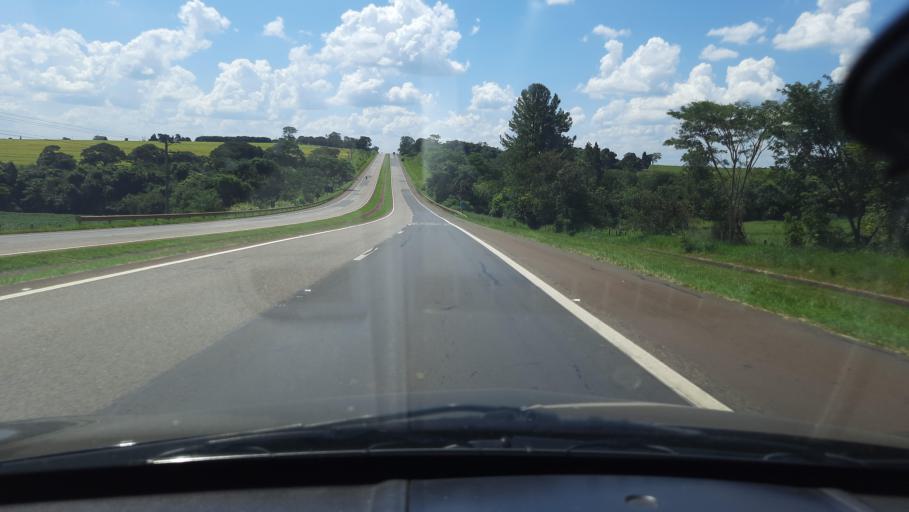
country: BR
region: Sao Paulo
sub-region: Casa Branca
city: Casa Branca
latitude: -21.7327
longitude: -47.0745
